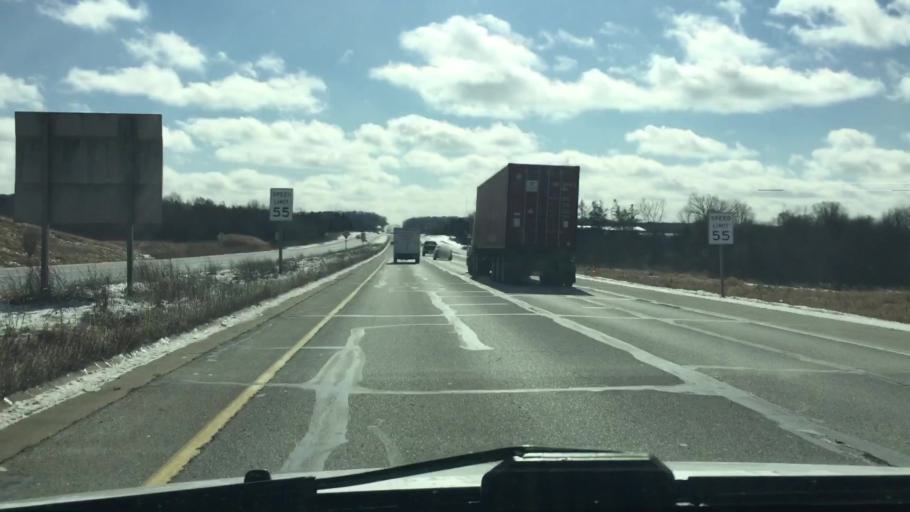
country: US
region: Wisconsin
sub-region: Waukesha County
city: Waukesha
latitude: 42.9581
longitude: -88.2281
